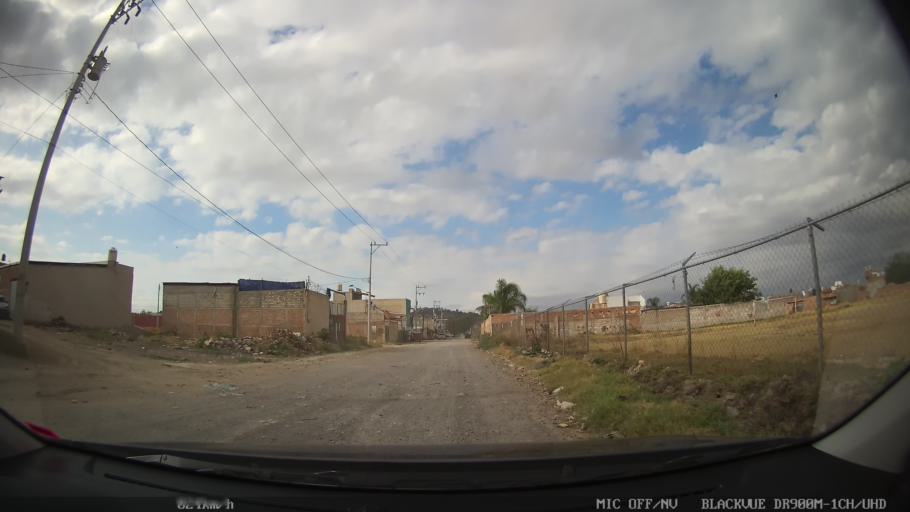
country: MX
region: Jalisco
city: Tonala
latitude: 20.6571
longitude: -103.2416
